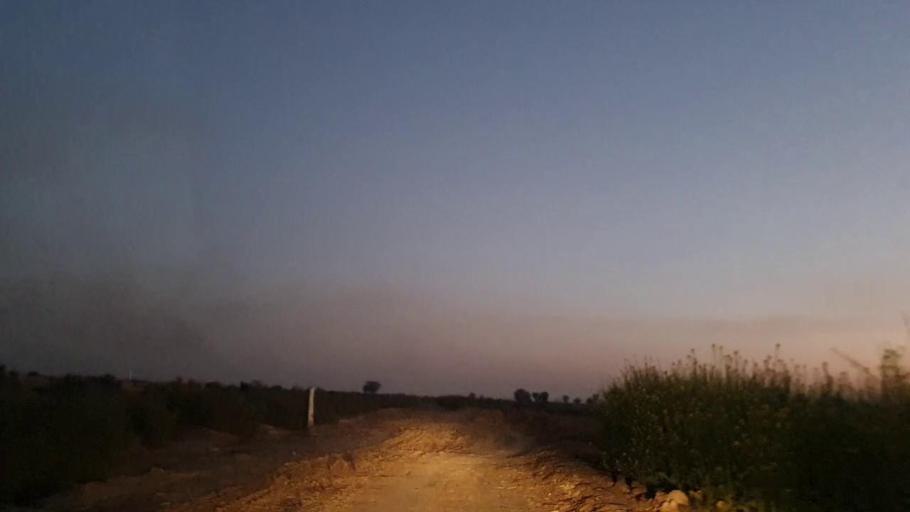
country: PK
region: Sindh
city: Nawabshah
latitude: 26.3312
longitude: 68.3749
